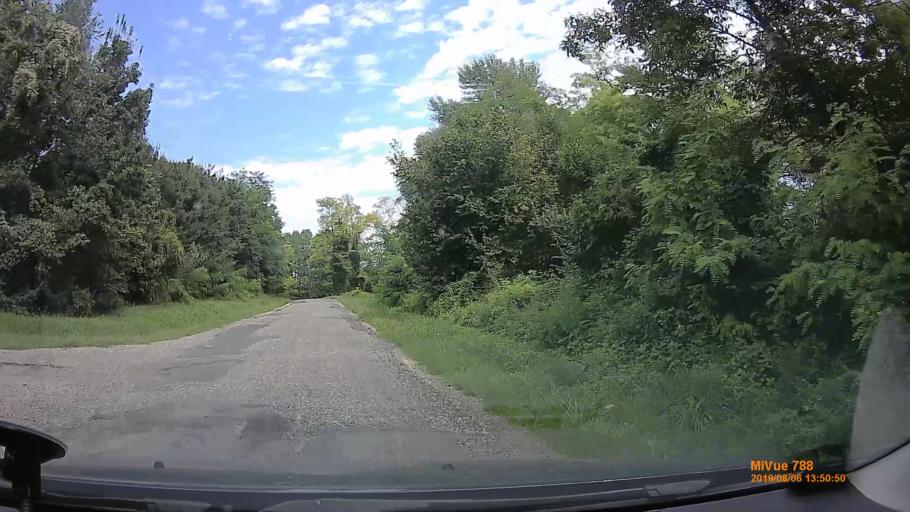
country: HU
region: Zala
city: Zalakomar
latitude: 46.5757
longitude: 17.1123
